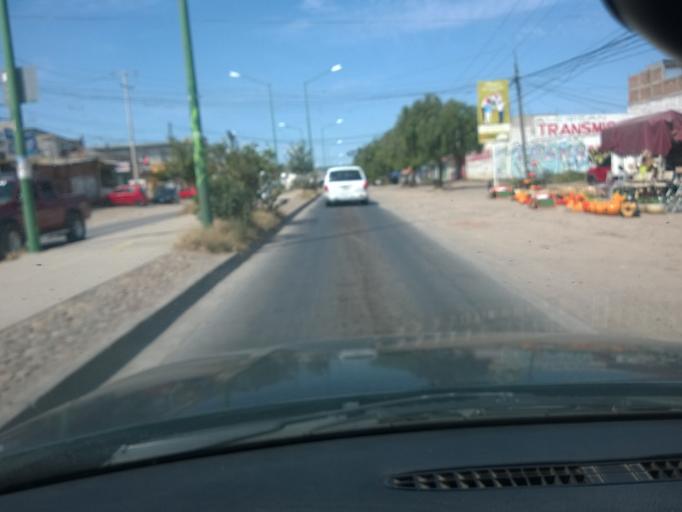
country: MX
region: Guanajuato
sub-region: Leon
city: Ejido la Joya
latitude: 21.1382
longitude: -101.7288
